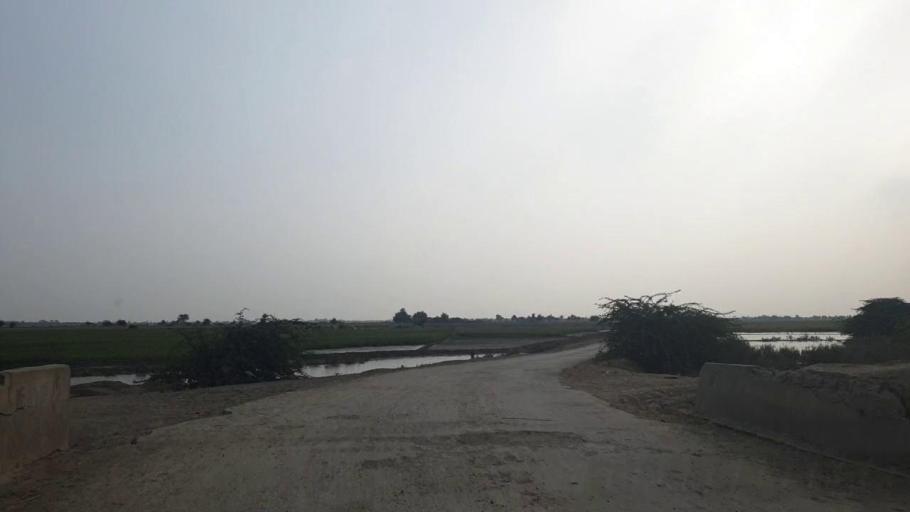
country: PK
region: Sindh
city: Badin
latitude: 24.6516
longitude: 68.7002
